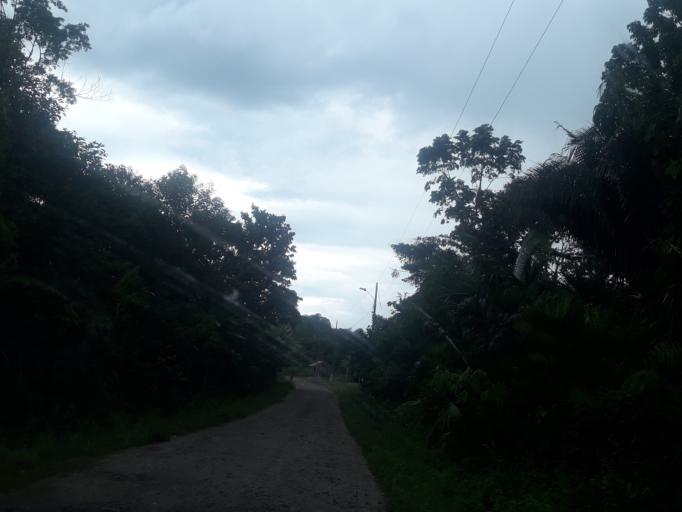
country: EC
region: Napo
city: Tena
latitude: -1.0982
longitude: -77.6825
